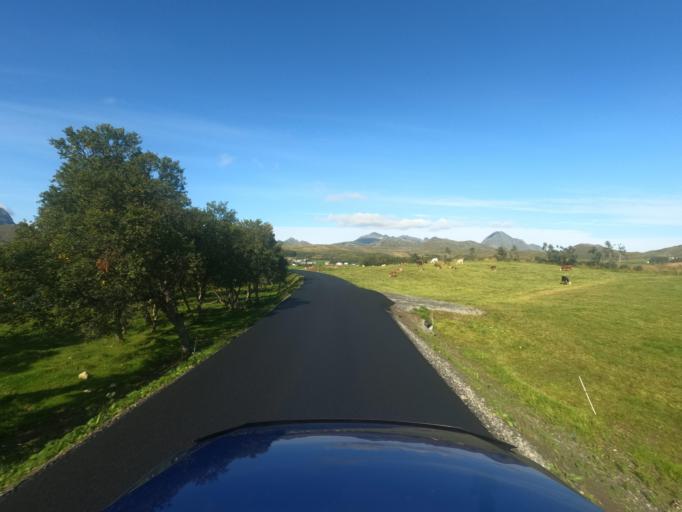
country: NO
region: Nordland
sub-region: Vestvagoy
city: Evjen
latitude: 68.2371
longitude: 13.7686
